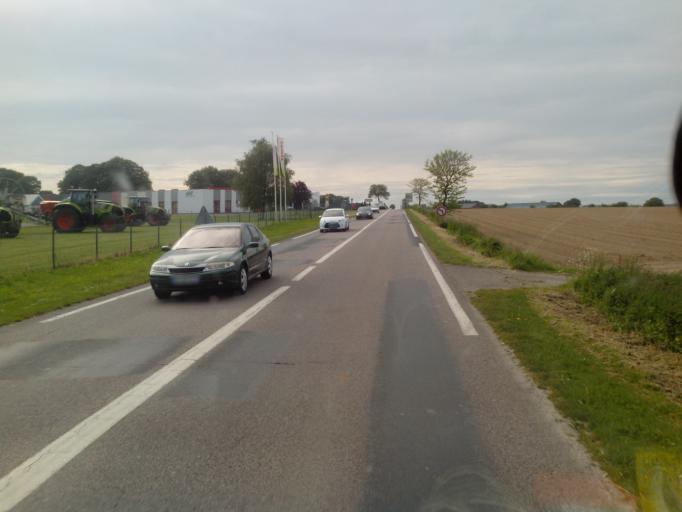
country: FR
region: Haute-Normandie
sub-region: Departement de la Seine-Maritime
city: Fauville-en-Caux
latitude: 49.6547
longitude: 0.5997
